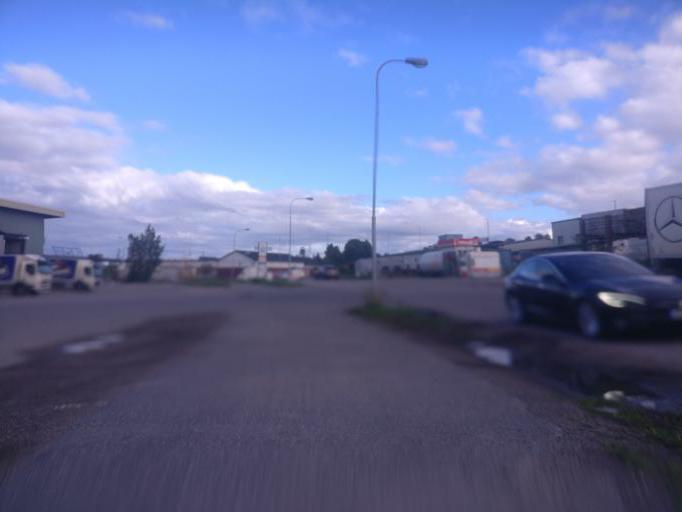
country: SE
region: Vaesternorrland
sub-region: Sundsvalls Kommun
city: Sundsvall
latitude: 62.3865
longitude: 17.3243
